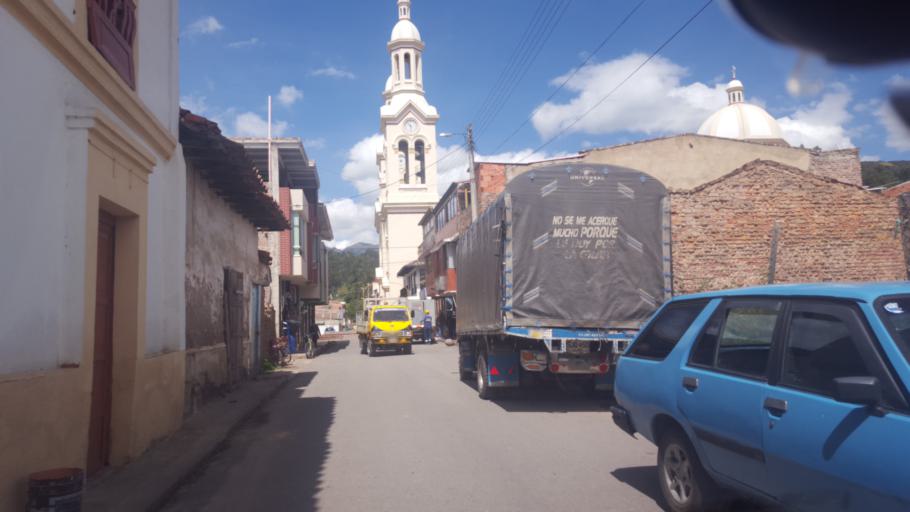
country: CO
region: Boyaca
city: Belen
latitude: 5.9903
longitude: -72.9125
